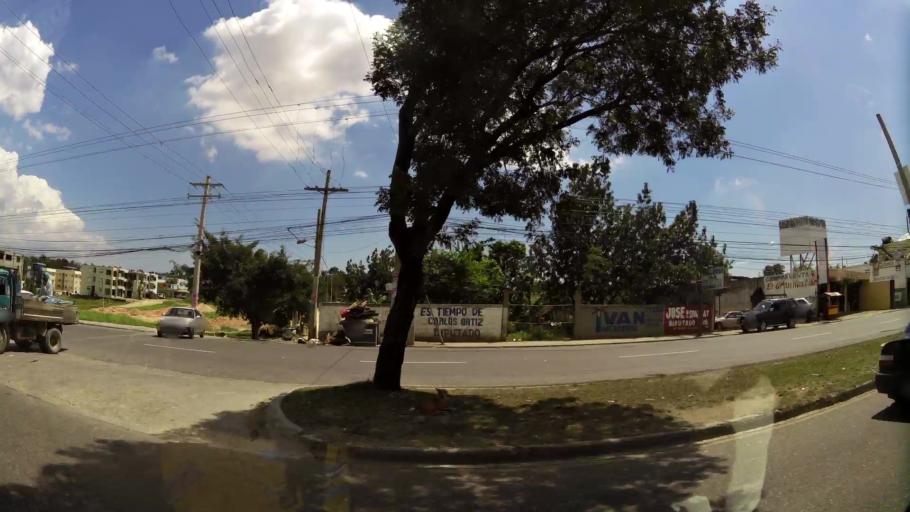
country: DO
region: Nacional
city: Ensanche Luperon
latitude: 18.5459
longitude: -69.8945
